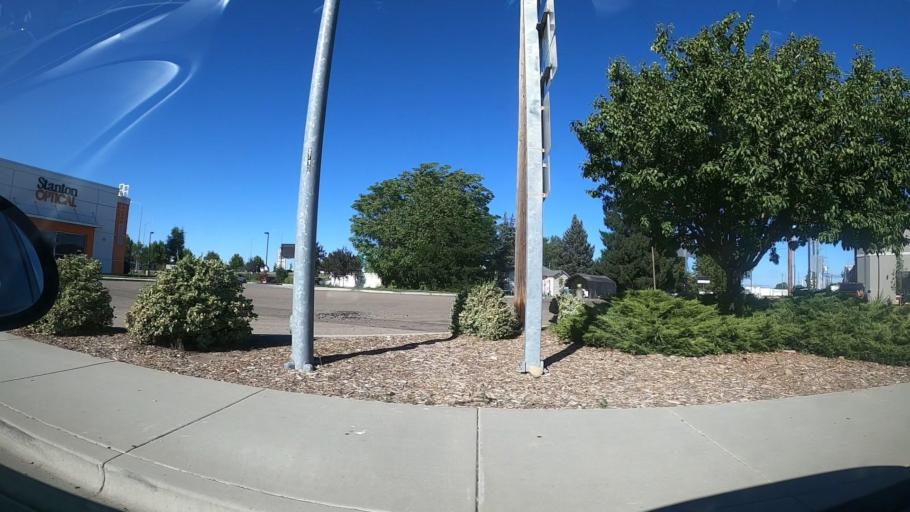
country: US
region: Idaho
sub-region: Canyon County
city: Nampa
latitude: 43.6035
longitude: -116.6000
